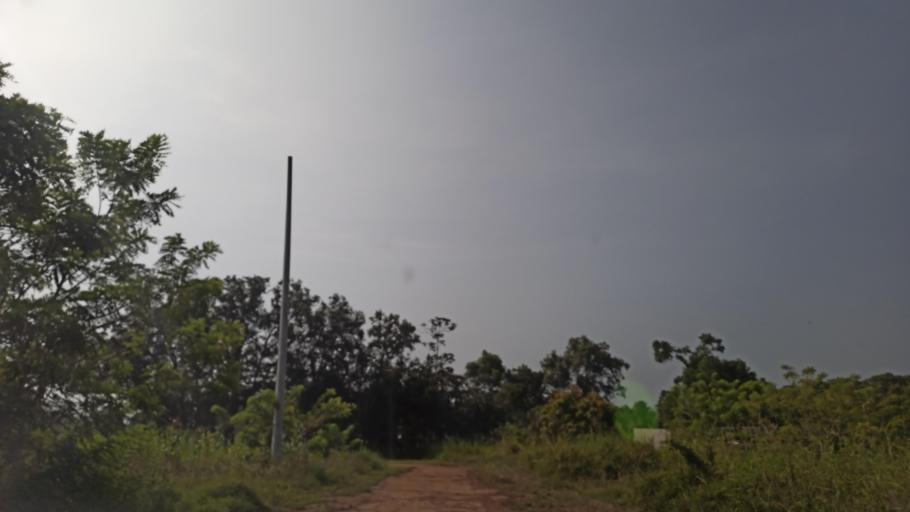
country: MX
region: Veracruz
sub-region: Martinez de la Torre
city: El Progreso
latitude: 20.1498
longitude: -97.0685
